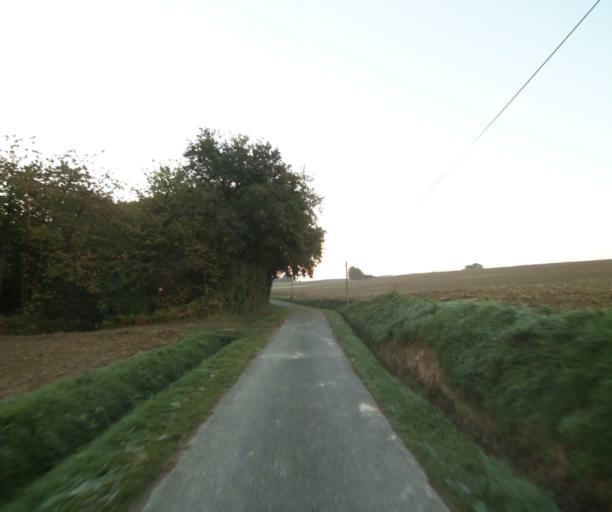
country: FR
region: Midi-Pyrenees
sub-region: Departement du Gers
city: Vic-Fezensac
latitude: 43.7803
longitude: 0.2228
